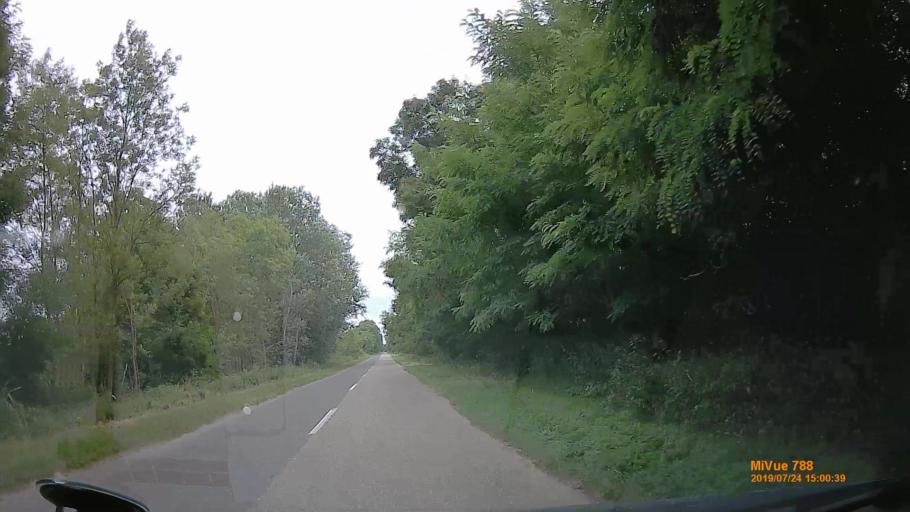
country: HU
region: Szabolcs-Szatmar-Bereg
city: Aranyosapati
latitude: 48.2317
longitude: 22.3739
